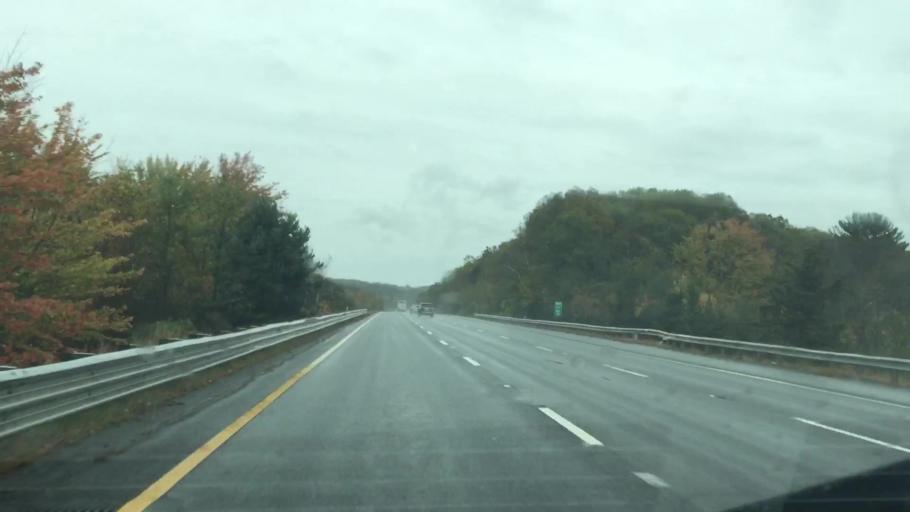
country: US
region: Massachusetts
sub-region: Essex County
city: Merrimac
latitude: 42.8219
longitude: -71.0143
